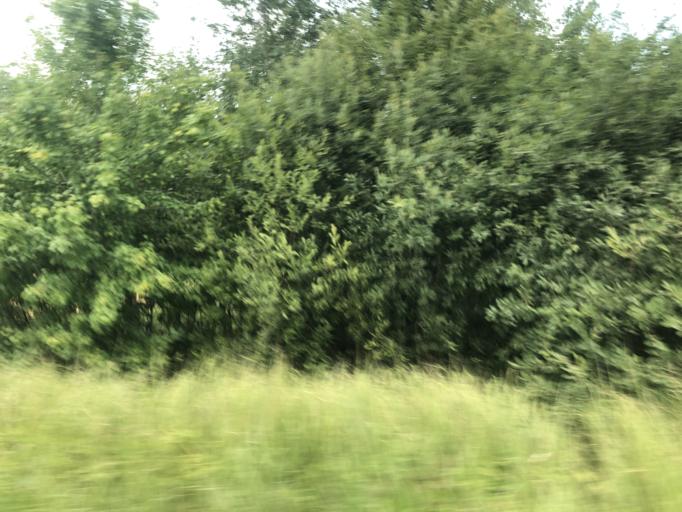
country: LV
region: Vecumnieki
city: Vecumnieki
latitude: 56.4607
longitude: 24.6649
